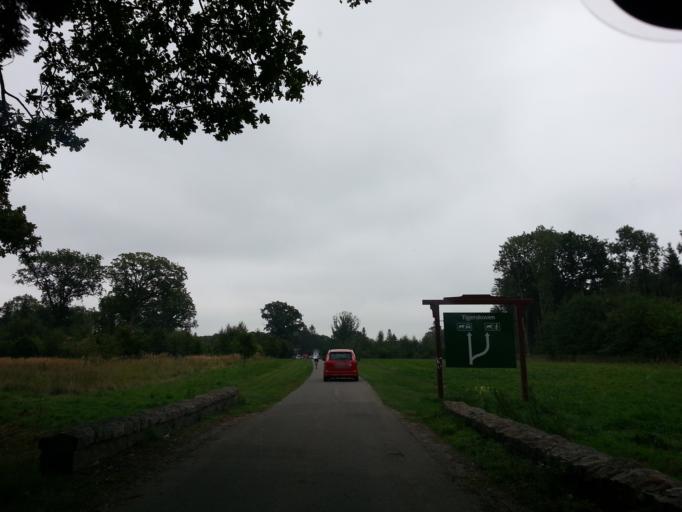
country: DK
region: Zealand
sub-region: Lolland Kommune
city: Maribo
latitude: 54.8200
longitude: 11.4921
